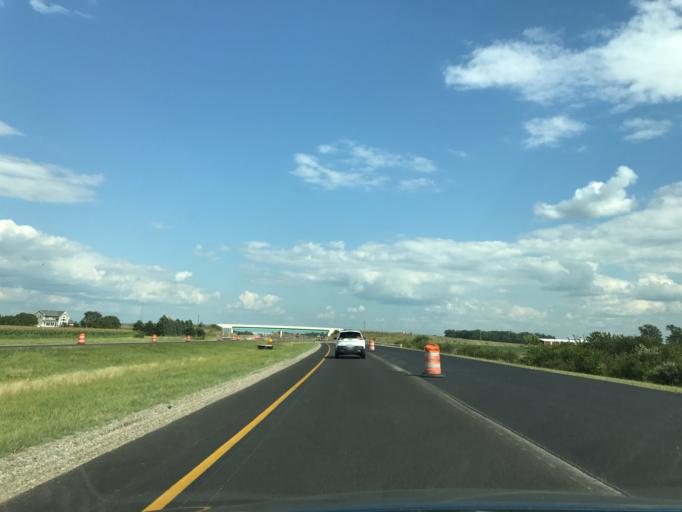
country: US
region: Ohio
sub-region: Van Wert County
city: Van Wert
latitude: 40.8701
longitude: -84.5092
